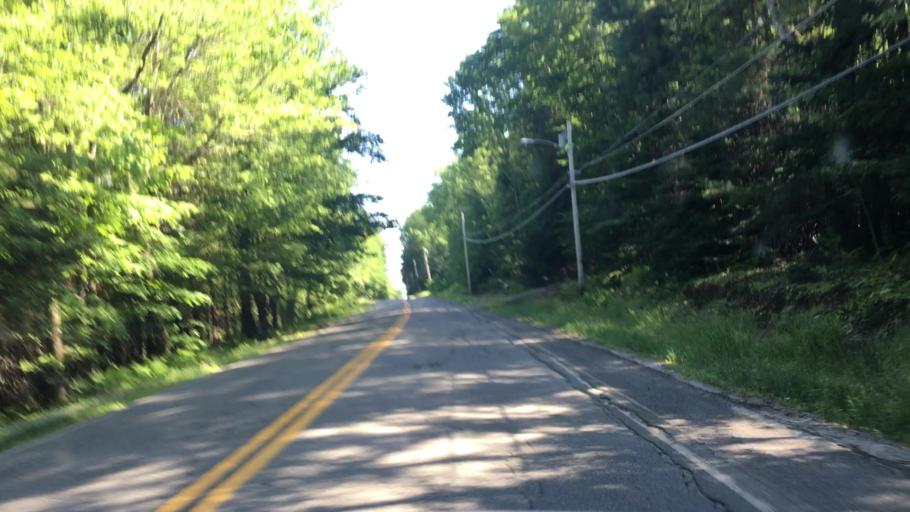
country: US
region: Maine
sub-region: Penobscot County
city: Enfield
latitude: 45.2691
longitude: -68.5617
